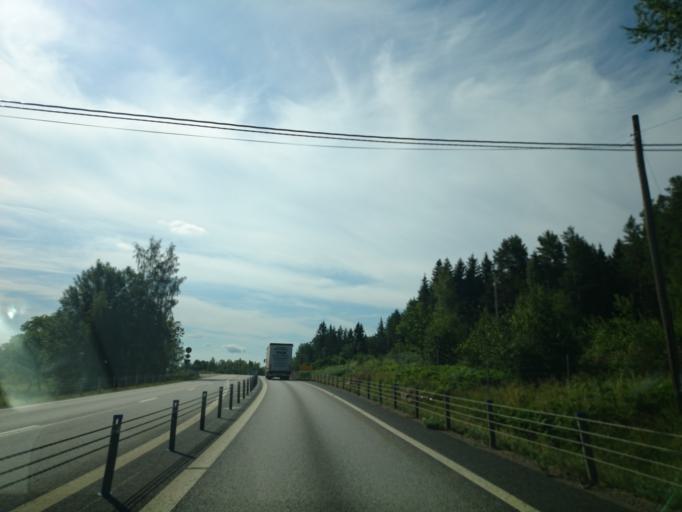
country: SE
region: Kalmar
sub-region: Vasterviks Kommun
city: Gamleby
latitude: 57.8517
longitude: 16.4311
